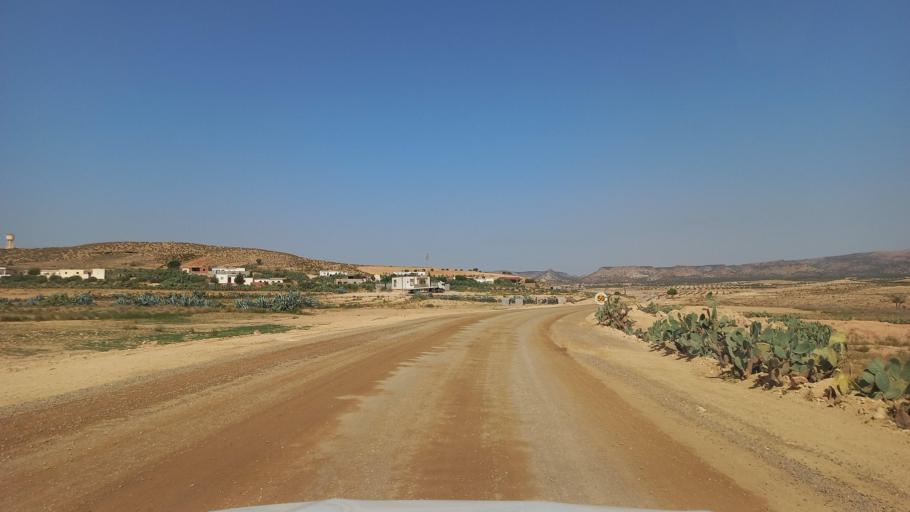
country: TN
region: Al Qasrayn
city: Sbiba
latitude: 35.3836
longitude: 9.0273
